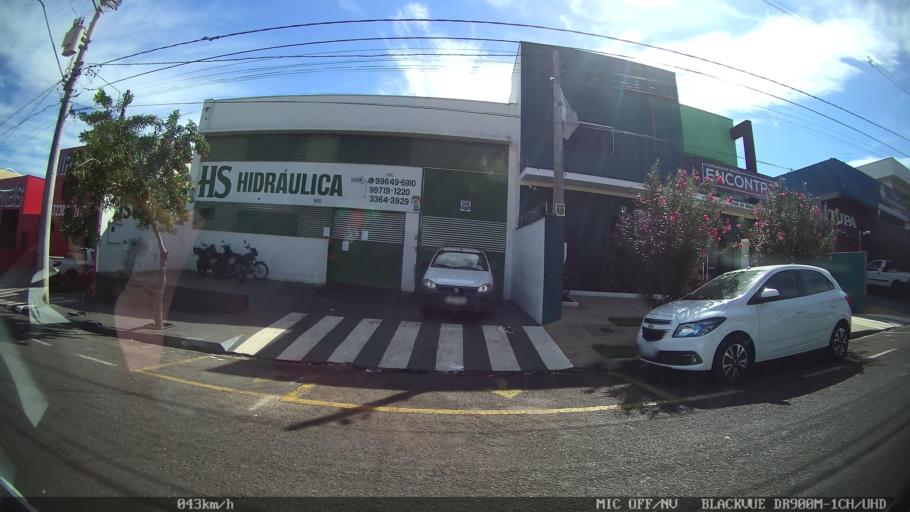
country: BR
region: Sao Paulo
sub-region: Sao Jose Do Rio Preto
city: Sao Jose do Rio Preto
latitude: -20.8415
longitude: -49.3610
